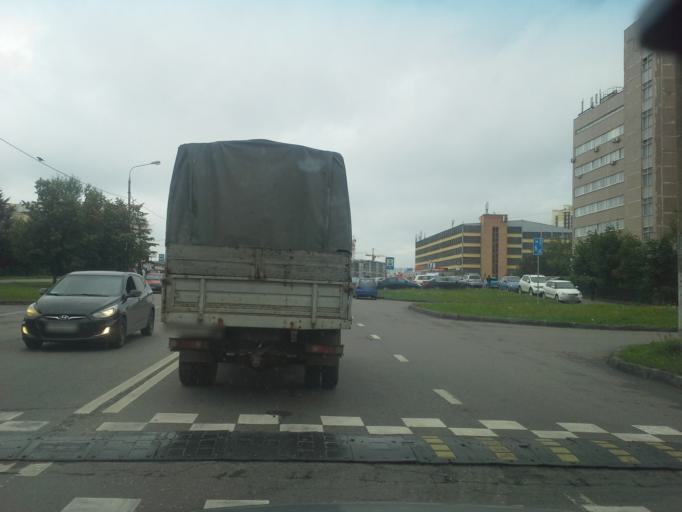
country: RU
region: Moscow
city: Novo-Peredelkino
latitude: 55.6390
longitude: 37.3415
